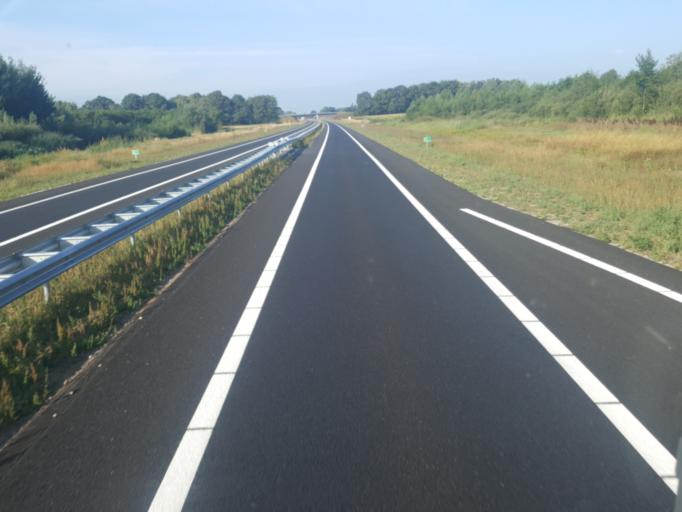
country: NL
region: Gelderland
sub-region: Berkelland
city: Eibergen
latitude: 52.1219
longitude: 6.6423
